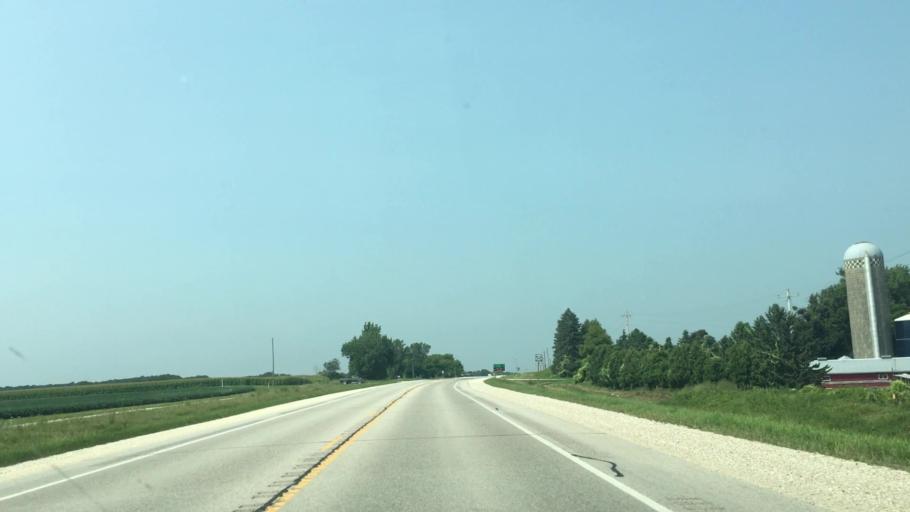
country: US
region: Iowa
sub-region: Winneshiek County
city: Decorah
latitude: 43.2020
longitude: -91.8767
